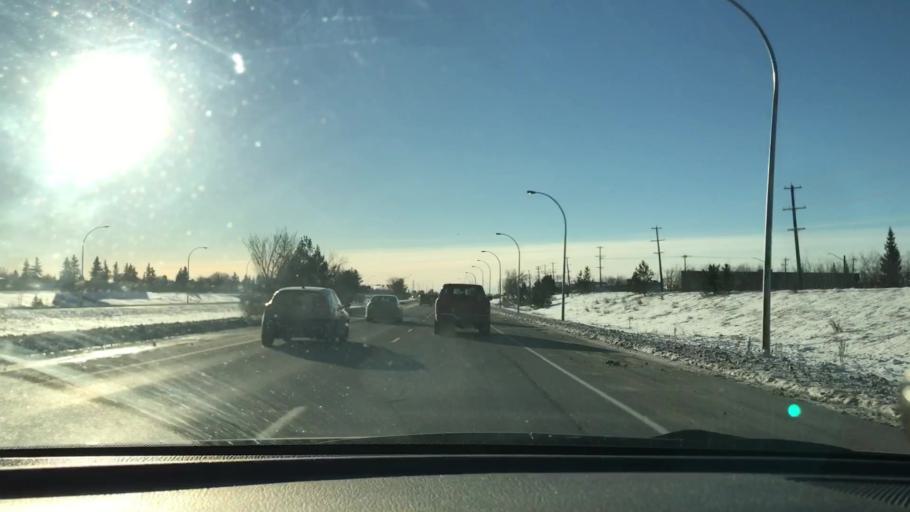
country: CA
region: Alberta
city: Edmonton
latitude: 53.4783
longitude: -113.4669
